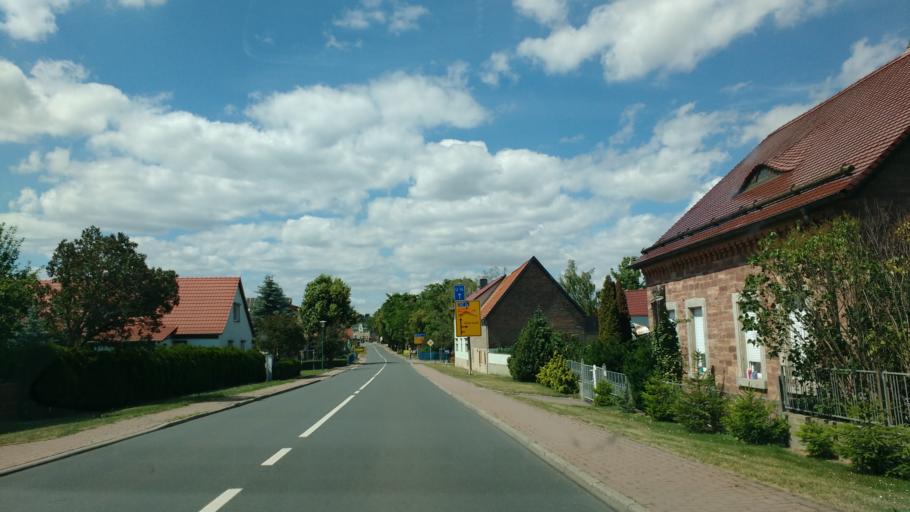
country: DE
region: Saxony-Anhalt
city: Farnstadt
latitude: 51.4249
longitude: 11.5696
